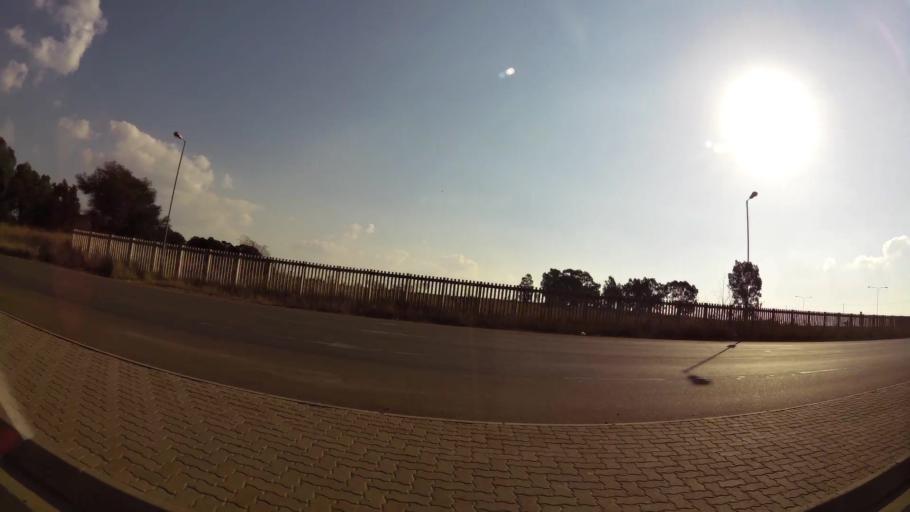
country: ZA
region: Gauteng
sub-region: City of Tshwane Metropolitan Municipality
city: Centurion
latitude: -25.9201
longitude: 28.2272
